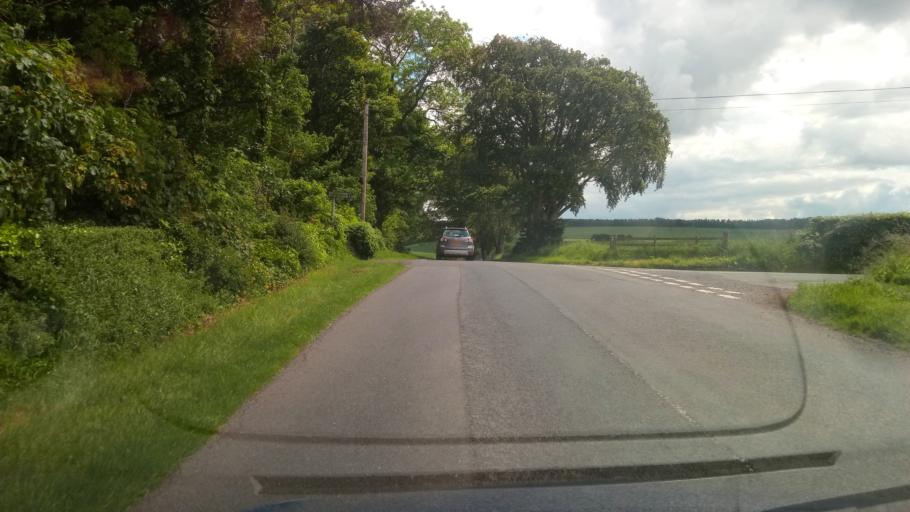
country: GB
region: Scotland
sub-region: The Scottish Borders
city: Coldstream
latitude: 55.6045
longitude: -2.3079
